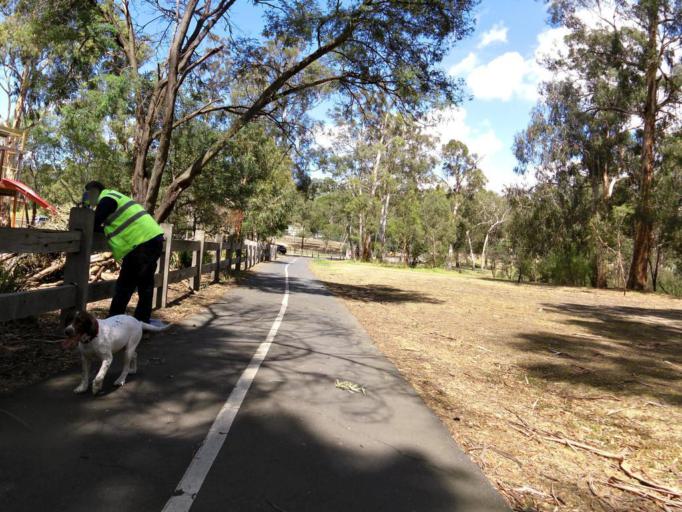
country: AU
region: Victoria
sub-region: Nillumbik
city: Eltham North
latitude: -37.6984
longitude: 145.1532
